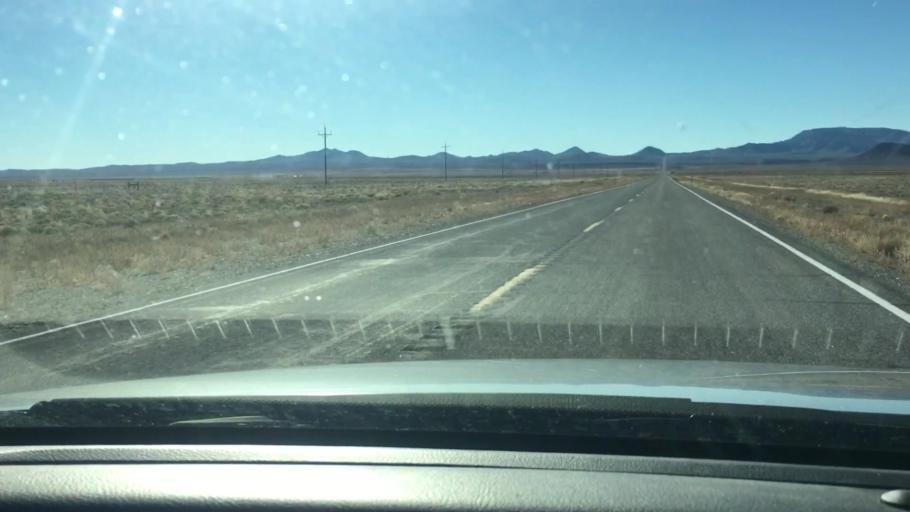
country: US
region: Nevada
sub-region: Nye County
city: Tonopah
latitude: 38.1510
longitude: -116.5699
